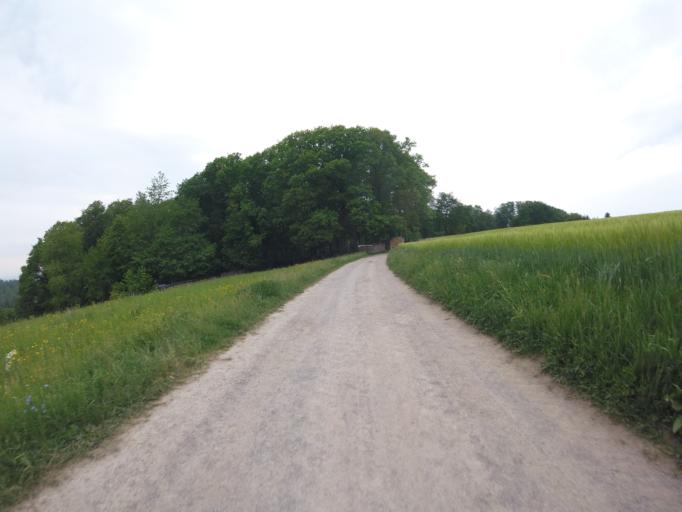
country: DE
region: Baden-Wuerttemberg
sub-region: Regierungsbezirk Stuttgart
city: Spiegelberg
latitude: 49.0372
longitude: 9.4074
